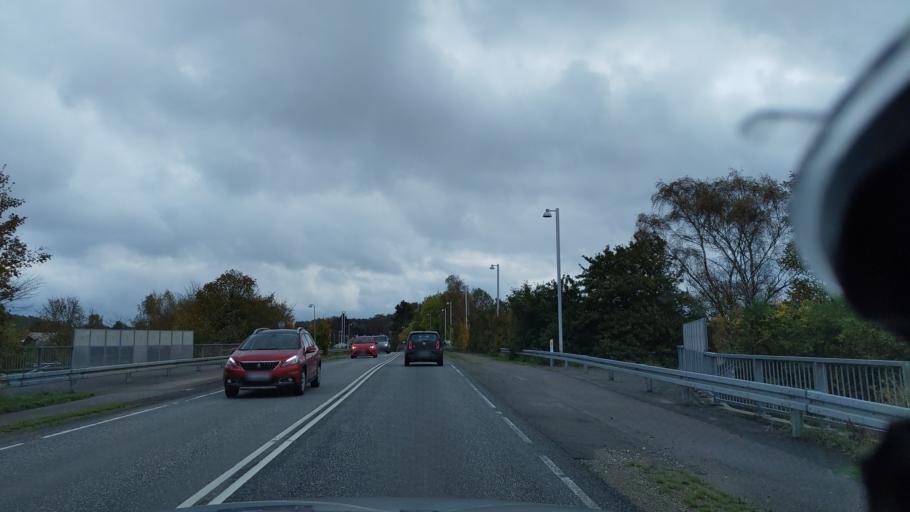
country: DK
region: Zealand
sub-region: Naestved Kommune
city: Fensmark
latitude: 55.2602
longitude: 11.8457
